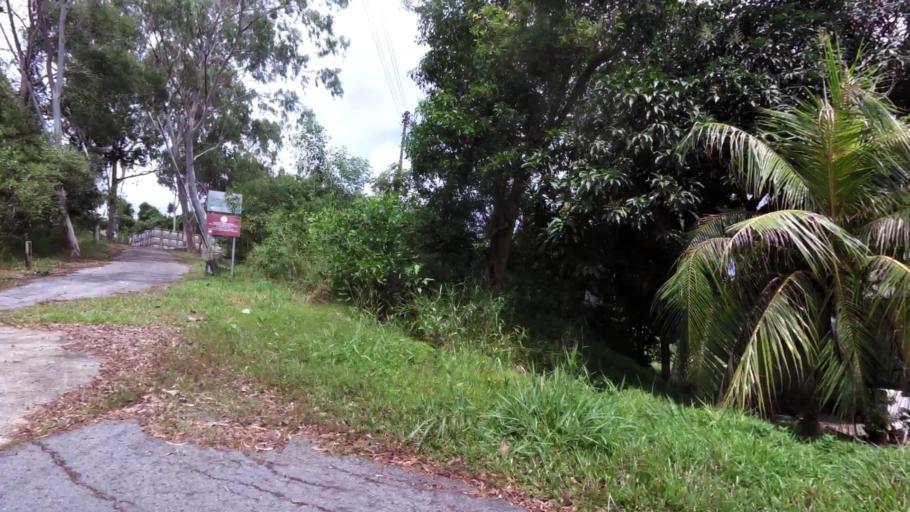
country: BN
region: Brunei and Muara
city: Bandar Seri Begawan
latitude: 4.9873
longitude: 114.9476
